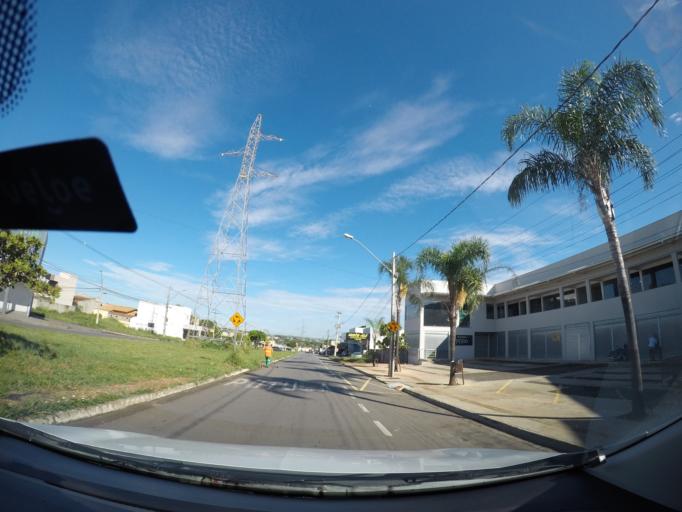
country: BR
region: Goias
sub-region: Goiania
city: Goiania
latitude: -16.7339
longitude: -49.3497
